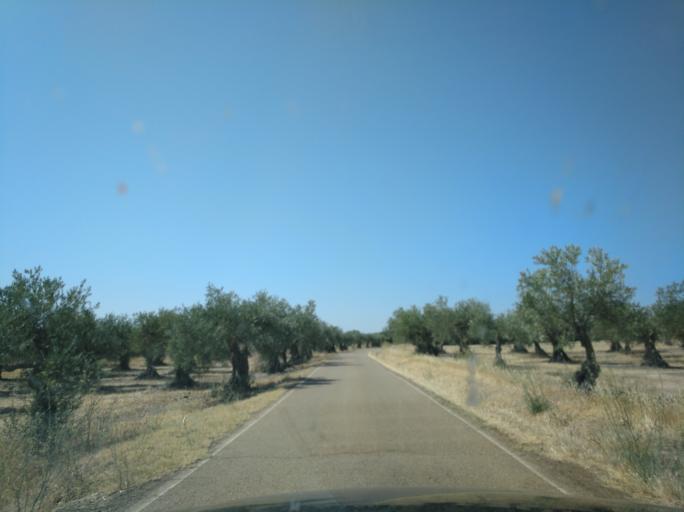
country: PT
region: Portalegre
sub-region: Campo Maior
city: Campo Maior
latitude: 39.0380
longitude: -7.0313
